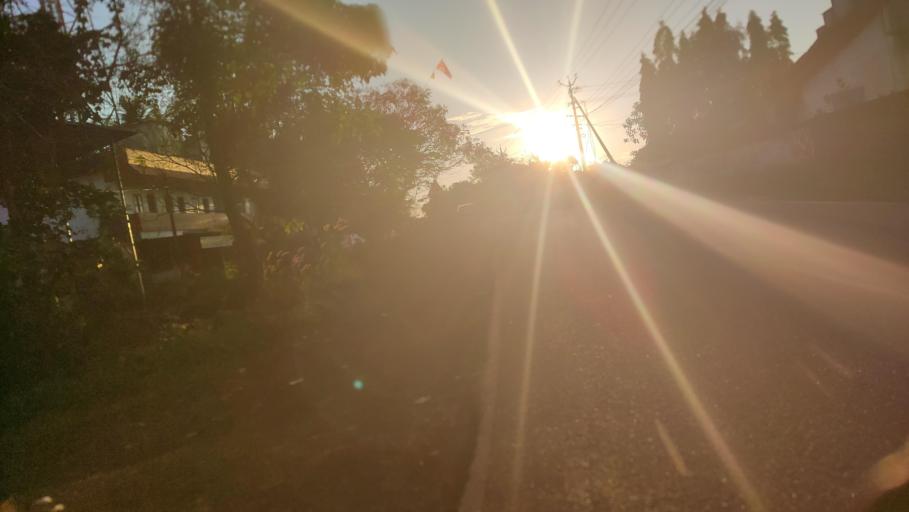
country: IN
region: Kerala
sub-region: Kasaragod District
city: Kannangad
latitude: 12.3987
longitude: 75.0612
